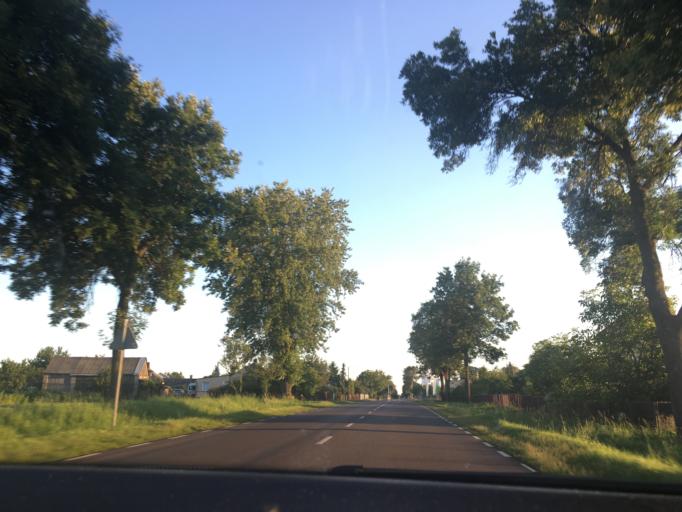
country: PL
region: Lublin Voivodeship
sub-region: Powiat radzynski
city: Radzyn Podlaski
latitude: 51.8261
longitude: 22.6803
